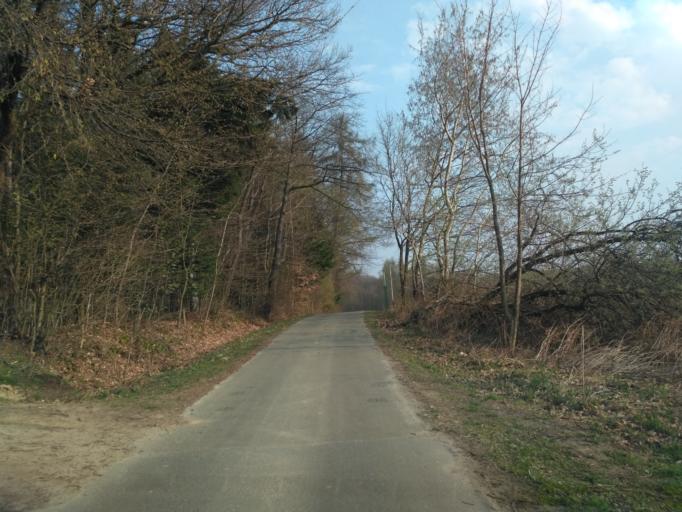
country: PL
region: Subcarpathian Voivodeship
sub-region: Powiat strzyzowski
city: Wisniowa
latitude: 49.8804
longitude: 21.6355
